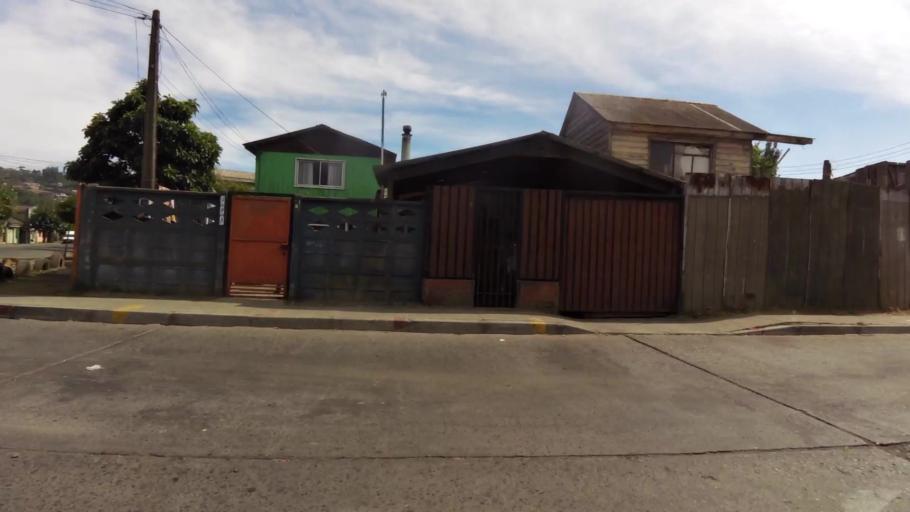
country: CL
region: Biobio
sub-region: Provincia de Concepcion
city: Talcahuano
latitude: -36.7257
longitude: -73.1234
